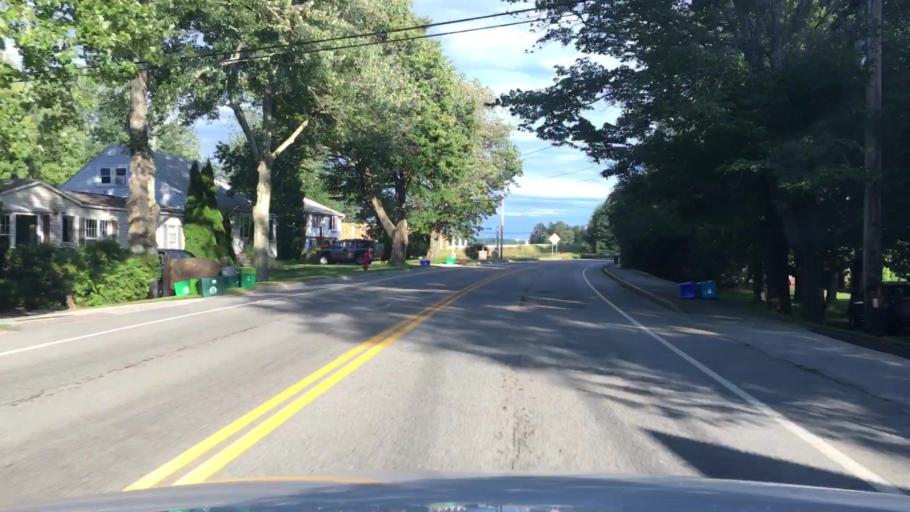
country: US
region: Maine
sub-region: York County
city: Eliot
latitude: 43.1276
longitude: -70.8415
